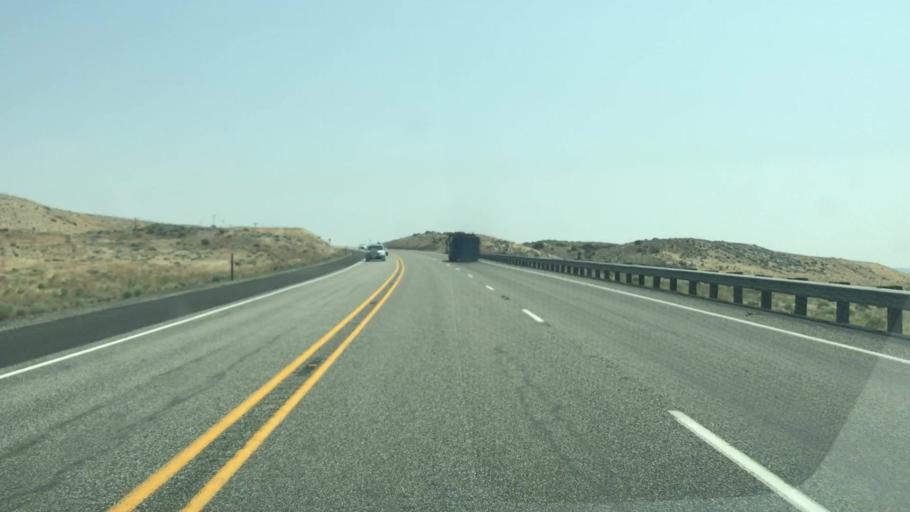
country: US
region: Washington
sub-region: Grant County
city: Quincy
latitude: 47.2365
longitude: -120.0590
